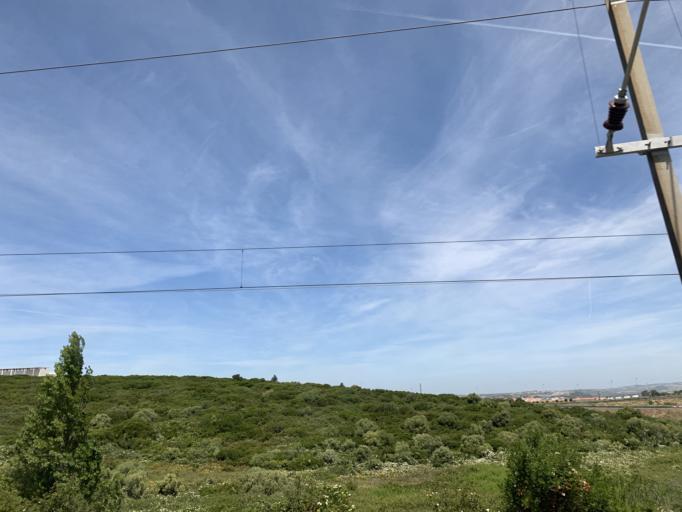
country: PT
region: Lisbon
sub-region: Sintra
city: Sintra
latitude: 38.8013
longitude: -9.3656
